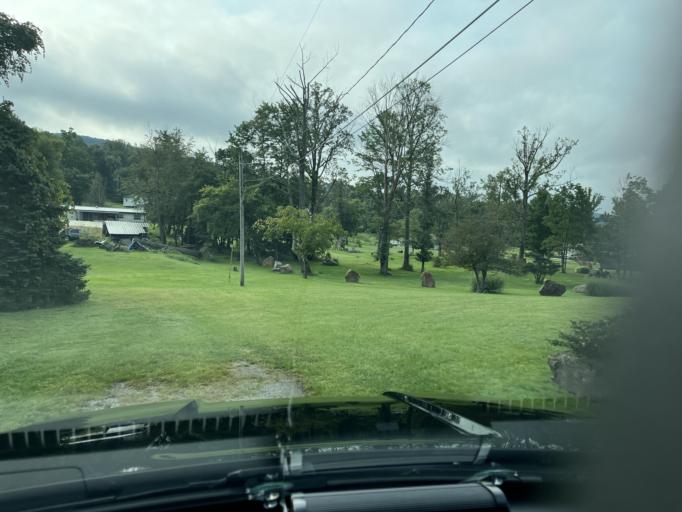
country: US
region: Pennsylvania
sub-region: Fayette County
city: Hopwood
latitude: 39.8678
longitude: -79.7013
